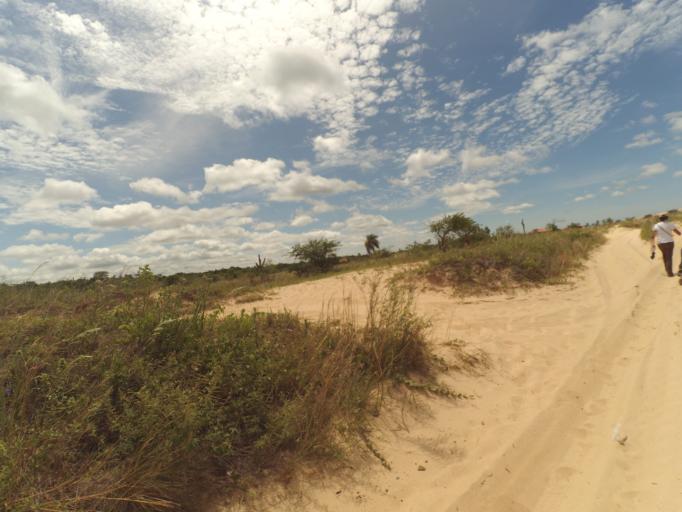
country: BO
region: Santa Cruz
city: Santa Cruz de la Sierra
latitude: -17.9309
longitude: -63.1605
